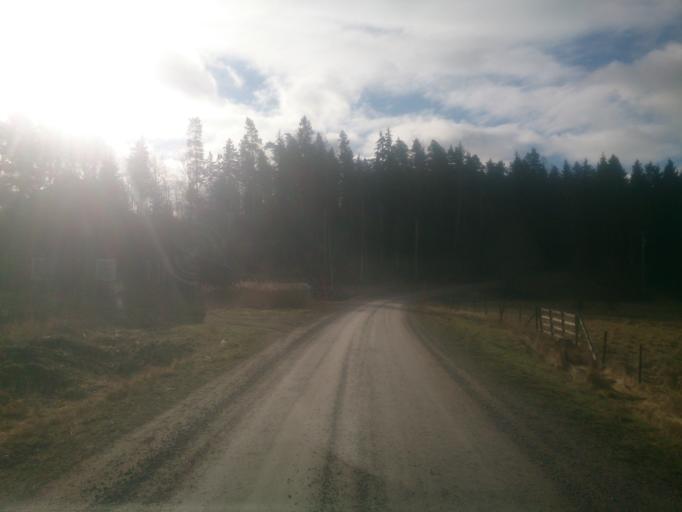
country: SE
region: OEstergoetland
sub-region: Atvidabergs Kommun
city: Atvidaberg
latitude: 58.2191
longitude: 16.1684
